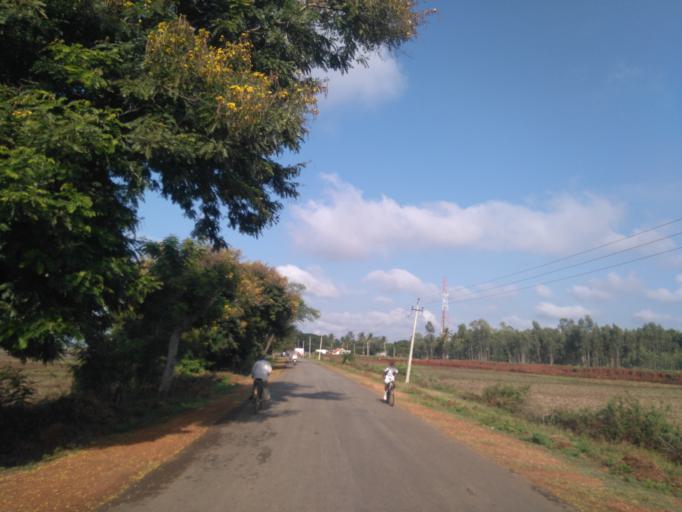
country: IN
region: Karnataka
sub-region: Mysore
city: Tirumakudal Narsipur
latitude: 12.2587
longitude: 77.0030
